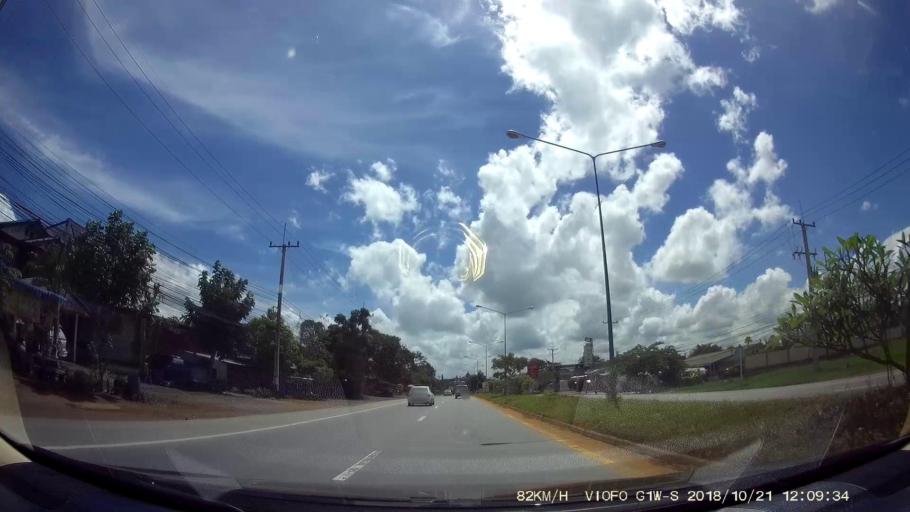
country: TH
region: Chaiyaphum
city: Chatturat
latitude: 15.4196
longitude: 101.8328
